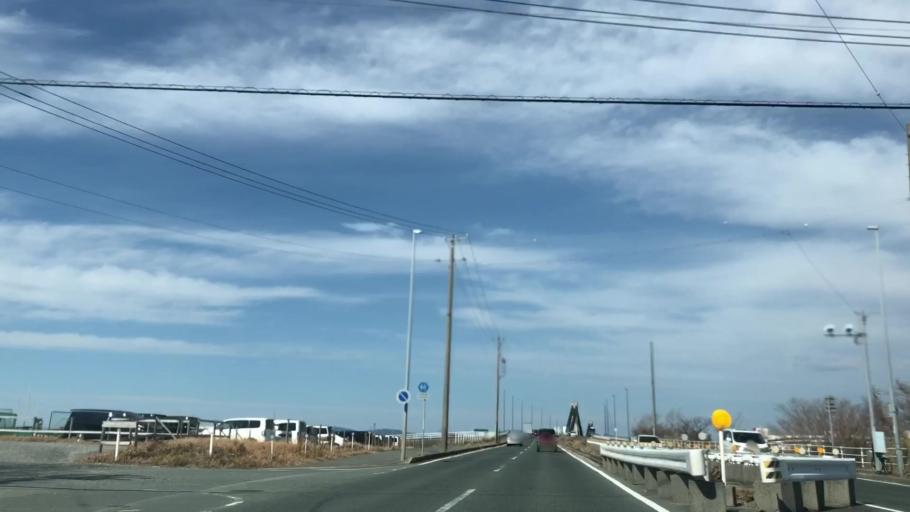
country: JP
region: Shizuoka
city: Hamamatsu
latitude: 34.6883
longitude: 137.6474
